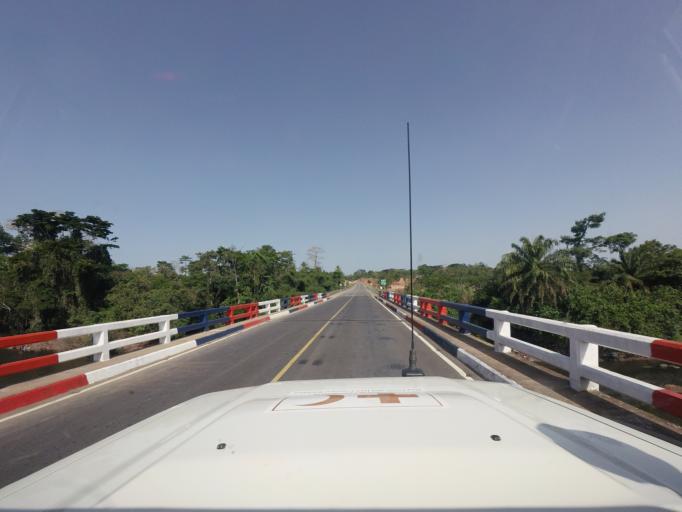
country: LR
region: Bong
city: Gbarnga
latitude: 7.0635
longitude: -9.1639
